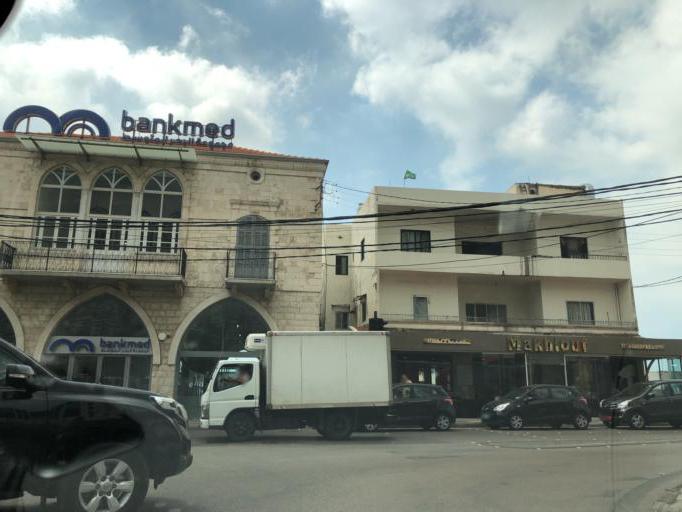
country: LB
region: Mont-Liban
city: Djounie
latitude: 33.9883
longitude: 35.6378
